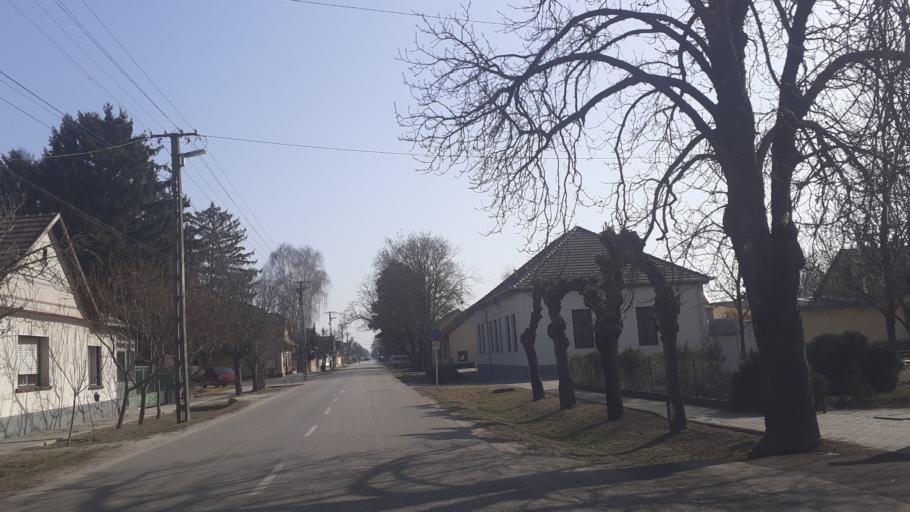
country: HU
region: Pest
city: Taborfalva
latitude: 47.0344
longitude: 19.4520
